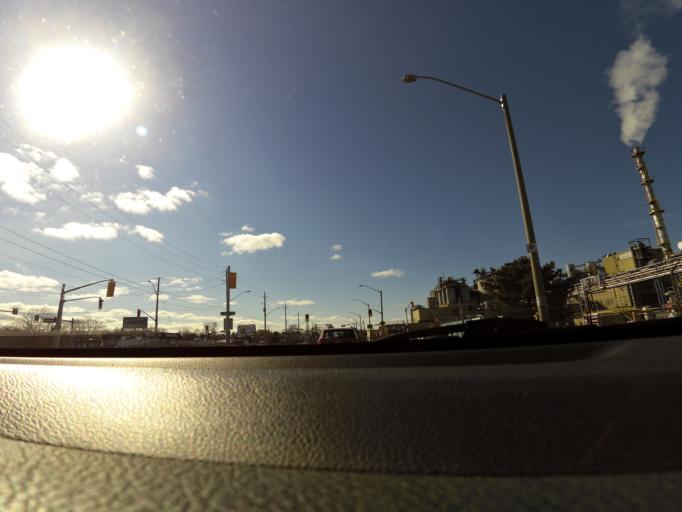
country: CA
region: Ontario
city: Hamilton
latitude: 43.2694
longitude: -79.8493
